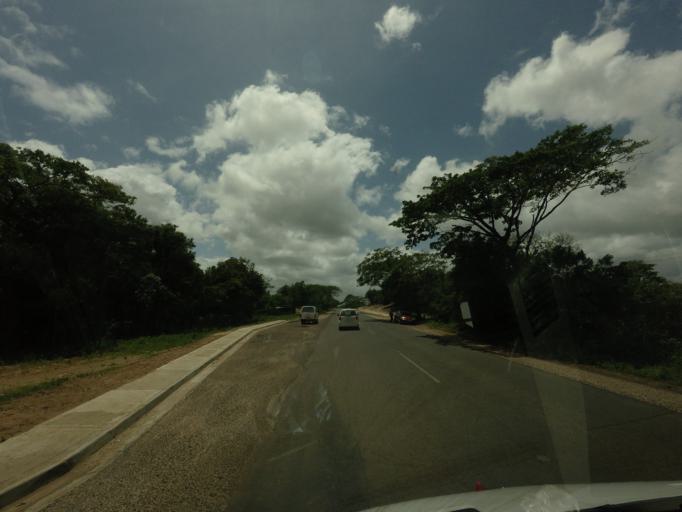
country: ZA
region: KwaZulu-Natal
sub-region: uMkhanyakude District Municipality
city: Mtubatuba
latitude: -28.3792
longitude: 32.3660
